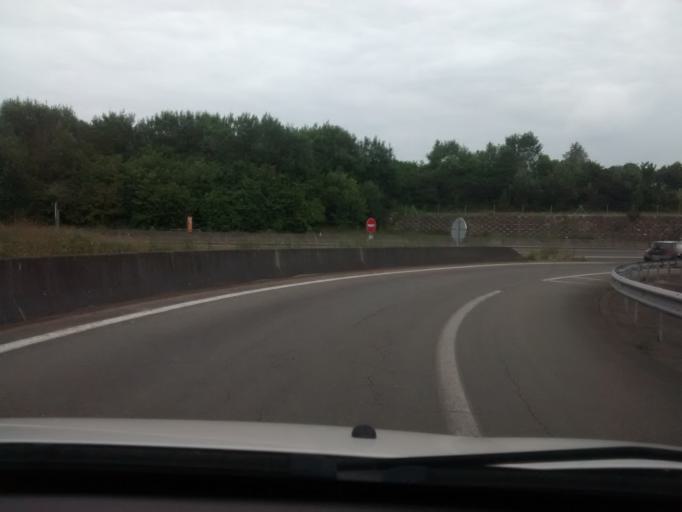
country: FR
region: Brittany
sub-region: Departement d'Ille-et-Vilaine
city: Liffre
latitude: 48.2047
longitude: -1.5267
